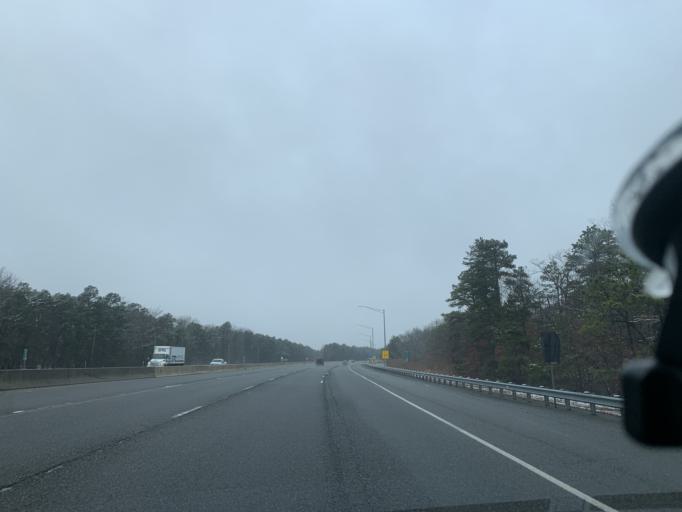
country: US
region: New Jersey
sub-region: Atlantic County
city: Pomona
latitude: 39.4455
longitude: -74.6177
